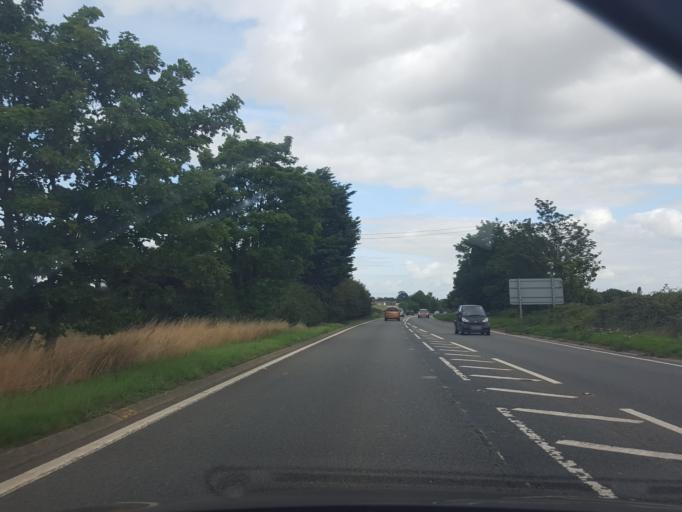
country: GB
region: England
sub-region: Essex
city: Mistley
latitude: 51.8995
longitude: 1.0723
